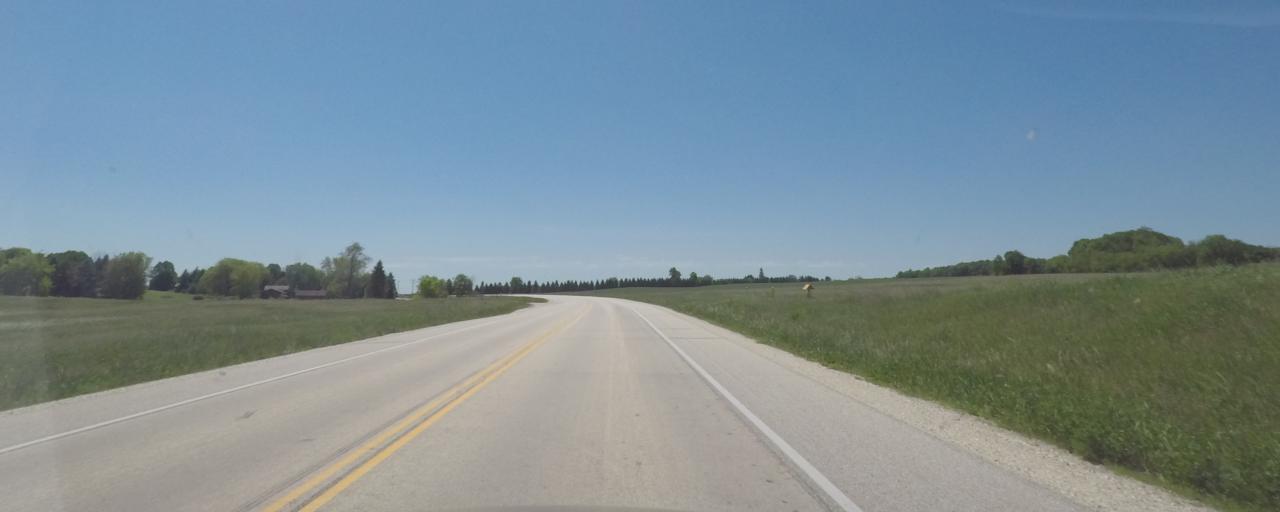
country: US
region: Wisconsin
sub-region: Washington County
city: West Bend
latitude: 43.4958
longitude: -88.1384
